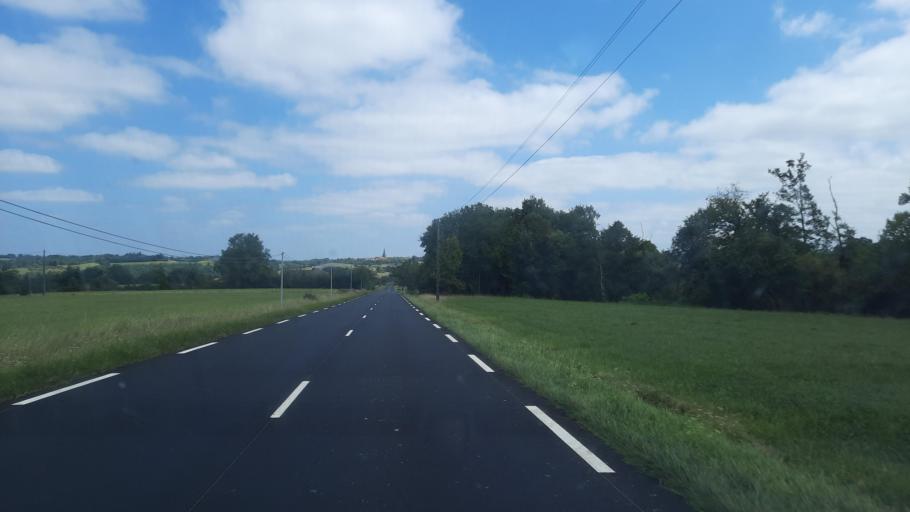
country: FR
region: Midi-Pyrenees
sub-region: Departement de la Haute-Garonne
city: Boulogne-sur-Gesse
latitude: 43.2976
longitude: 0.6143
